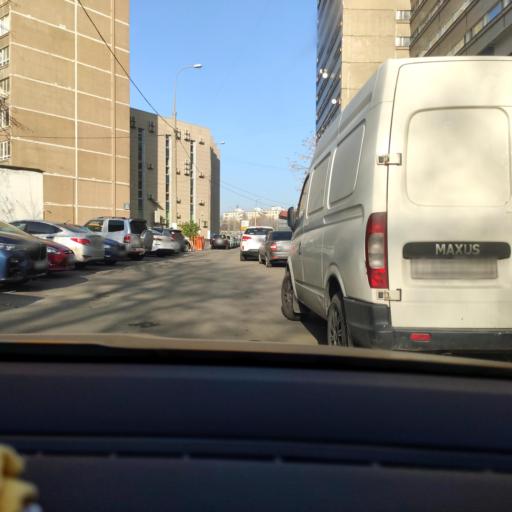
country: RU
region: Moscow
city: Vatutino
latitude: 55.8606
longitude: 37.6949
